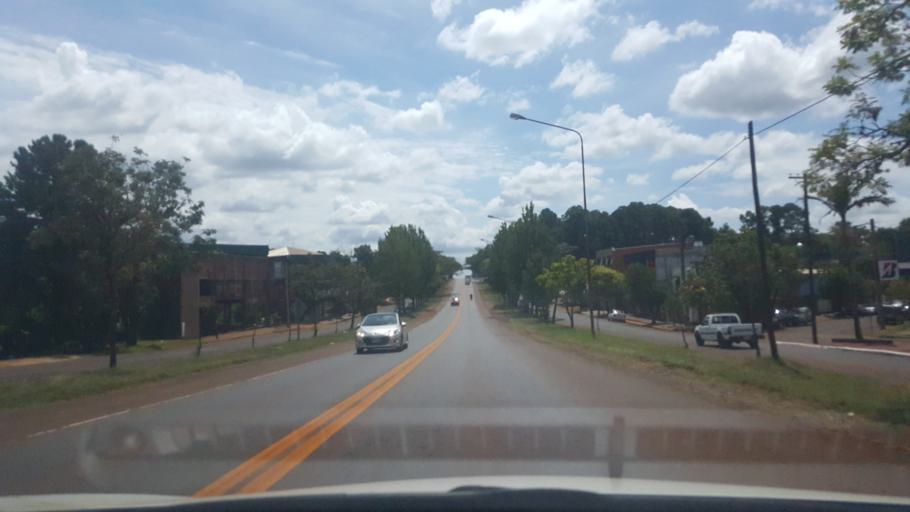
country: AR
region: Misiones
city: Jardin America
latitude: -27.0421
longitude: -55.2333
